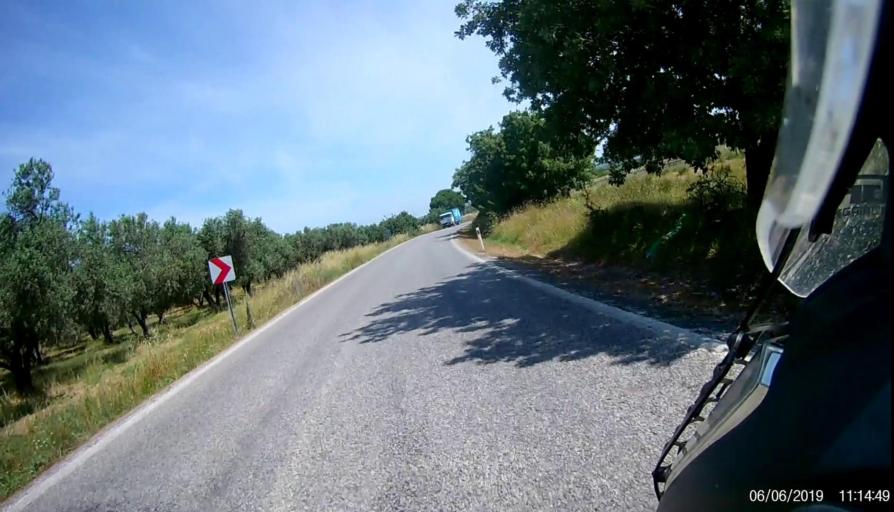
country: TR
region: Canakkale
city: Gulpinar
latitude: 39.6259
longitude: 26.1807
